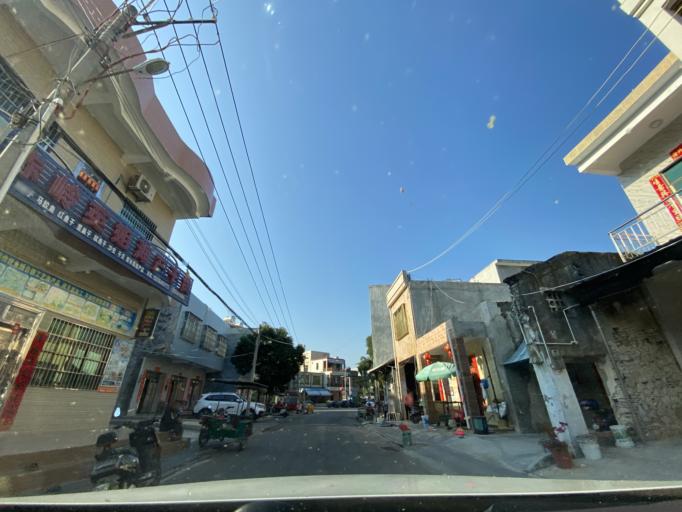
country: CN
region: Hainan
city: Yingzhou
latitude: 18.3889
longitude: 109.8185
